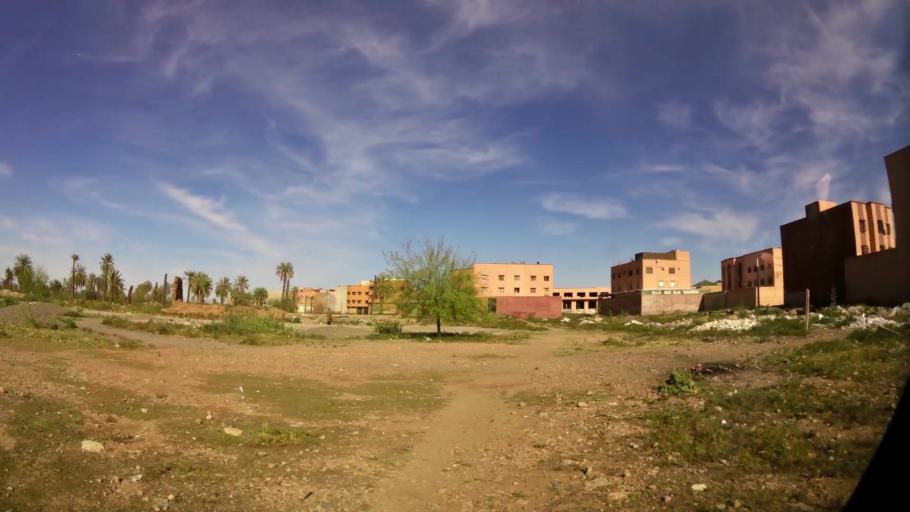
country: MA
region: Marrakech-Tensift-Al Haouz
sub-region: Marrakech
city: Marrakesh
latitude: 31.6789
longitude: -8.0391
